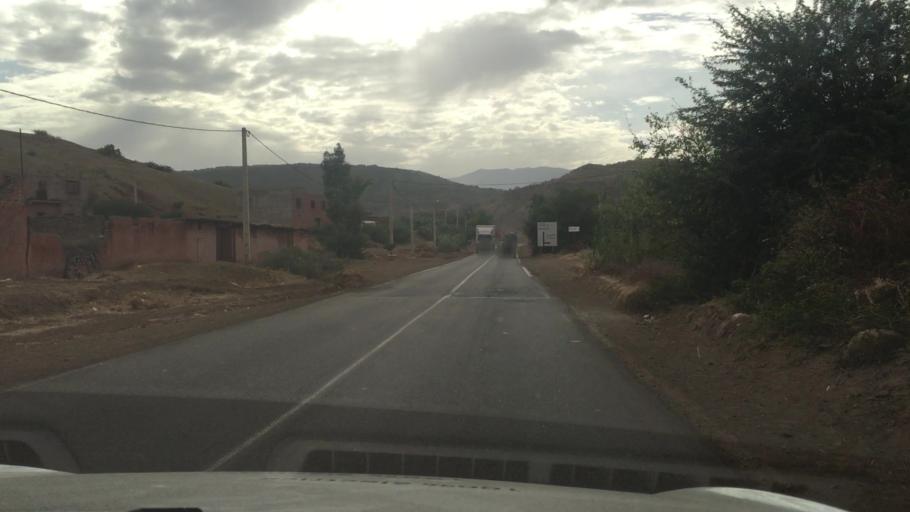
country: MA
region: Marrakech-Tensift-Al Haouz
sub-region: Al-Haouz
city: Touama
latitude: 31.5483
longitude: -7.5755
